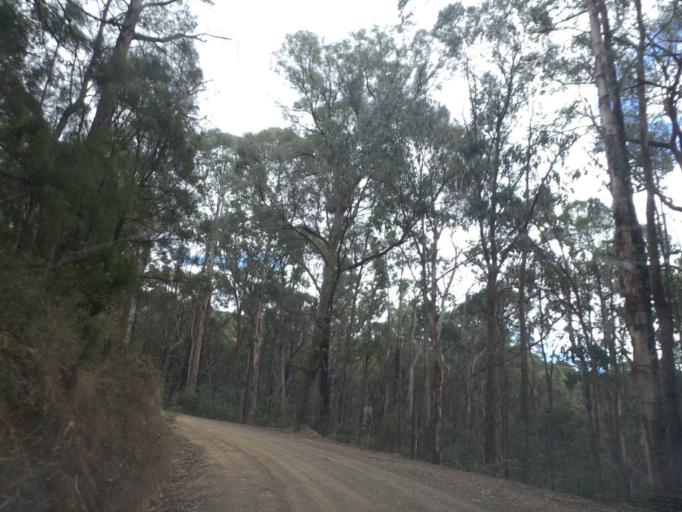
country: AU
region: Victoria
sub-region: Murrindindi
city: Alexandra
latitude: -37.4265
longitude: 145.9737
